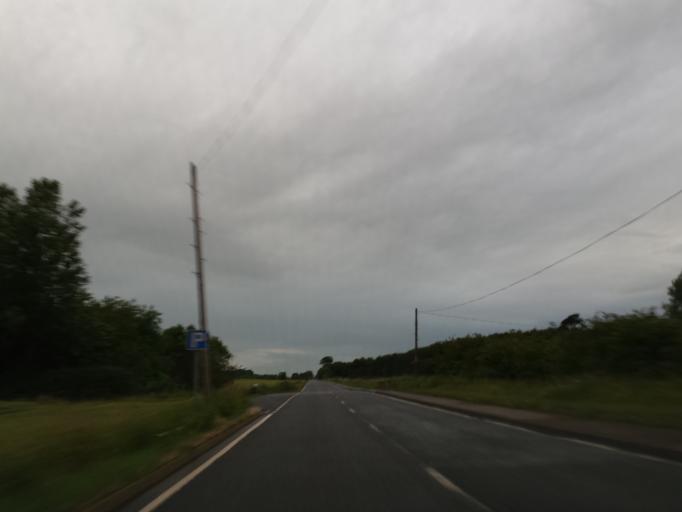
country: GB
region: Scotland
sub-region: East Lothian
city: Dunbar
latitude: 55.9905
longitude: -2.5778
